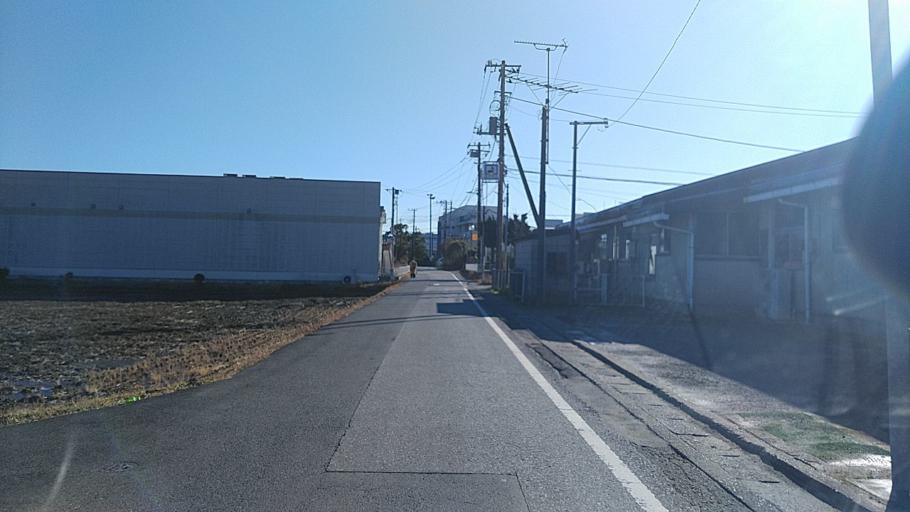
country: JP
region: Chiba
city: Kimitsu
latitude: 35.3050
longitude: 139.9566
